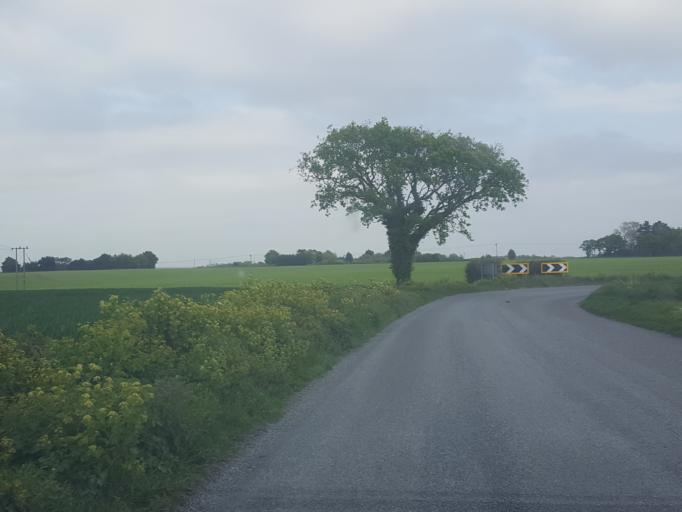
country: GB
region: England
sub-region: Essex
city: Frinton-on-Sea
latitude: 51.8529
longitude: 1.1952
